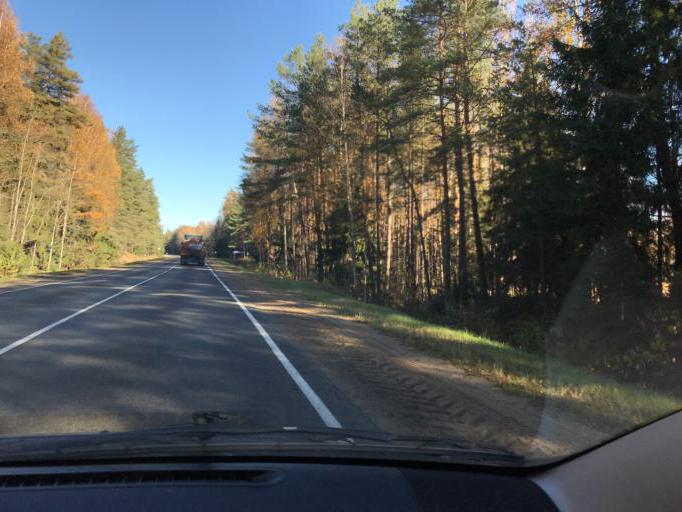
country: BY
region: Vitebsk
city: Polatsk
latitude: 55.3560
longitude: 28.8040
